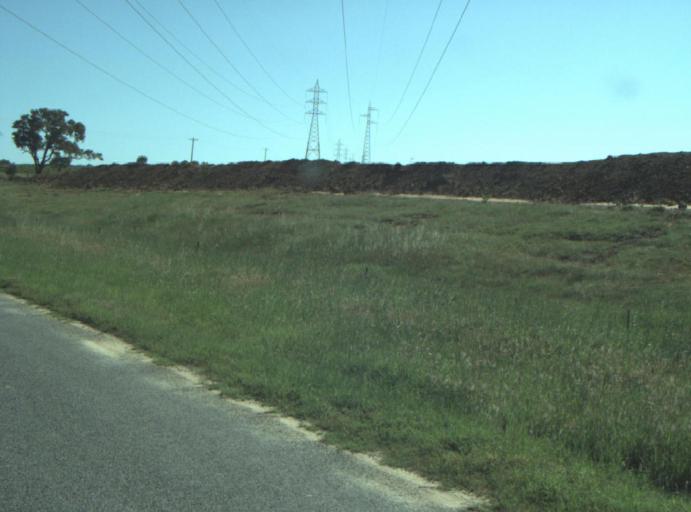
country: AU
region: Victoria
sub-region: Greater Geelong
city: Lara
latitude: -37.9297
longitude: 144.3947
